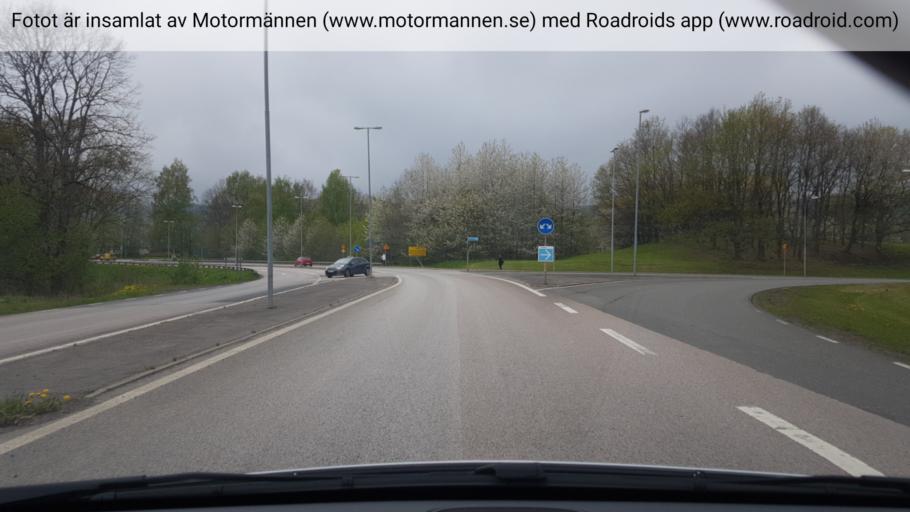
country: SE
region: Vaestra Goetaland
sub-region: Skovde Kommun
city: Skoevde
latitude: 58.4240
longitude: 13.8506
